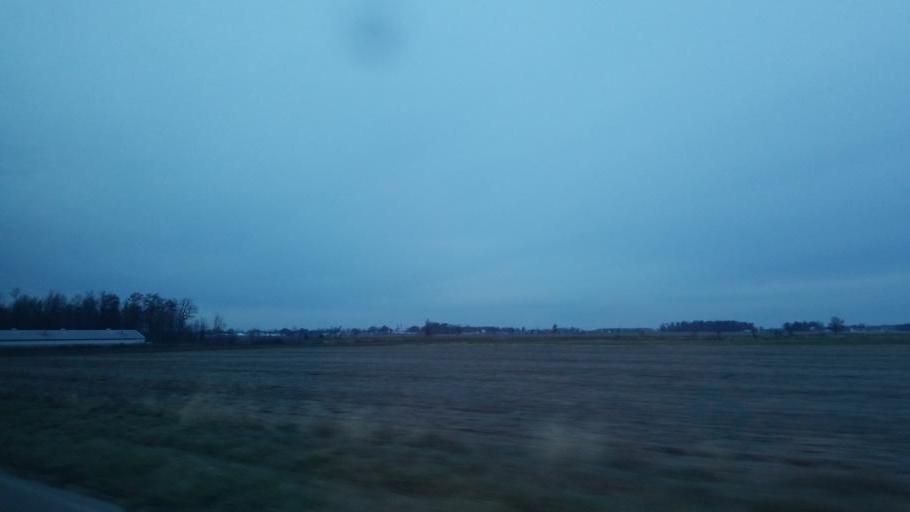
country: US
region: Indiana
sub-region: Adams County
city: Berne
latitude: 40.7314
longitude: -84.9210
